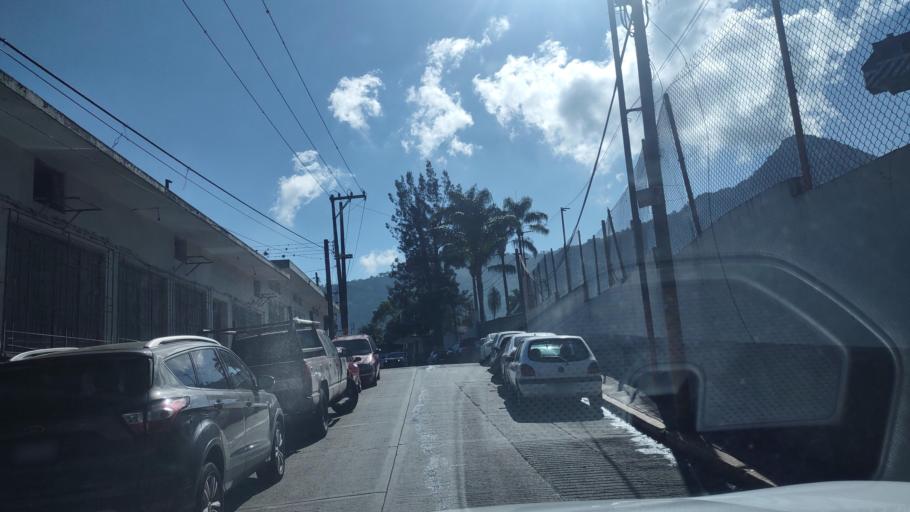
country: MX
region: Veracruz
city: Cuautlapan
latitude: 18.8735
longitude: -97.0238
